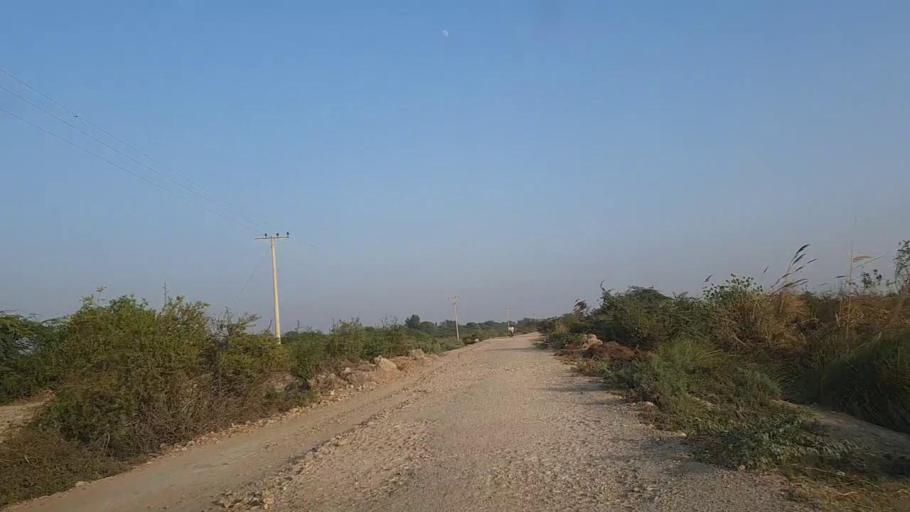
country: PK
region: Sindh
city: Keti Bandar
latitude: 24.2763
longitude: 67.6634
